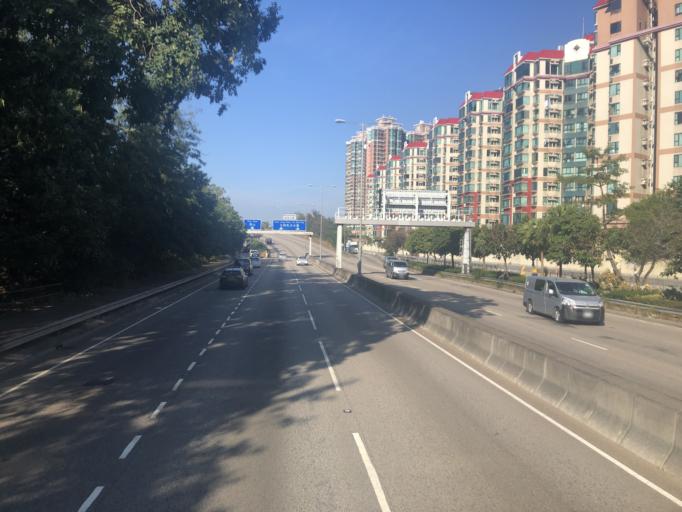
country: HK
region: Yuen Long
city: Yuen Long Kau Hui
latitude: 22.4411
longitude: 114.0162
